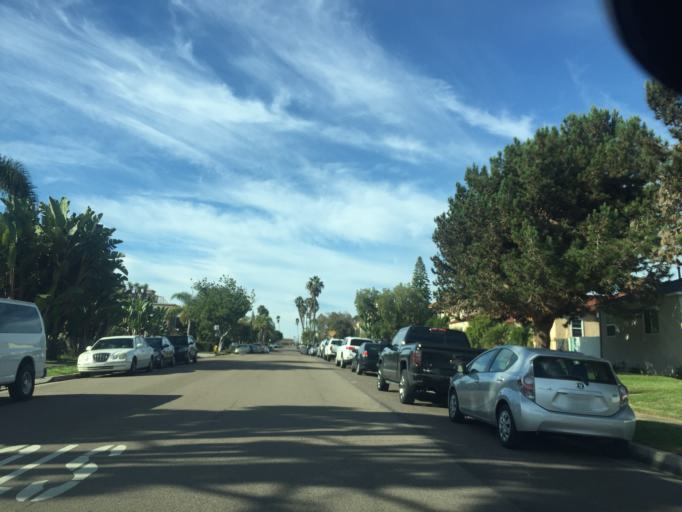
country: US
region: California
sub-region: San Diego County
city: La Jolla
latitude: 32.8028
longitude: -117.2320
